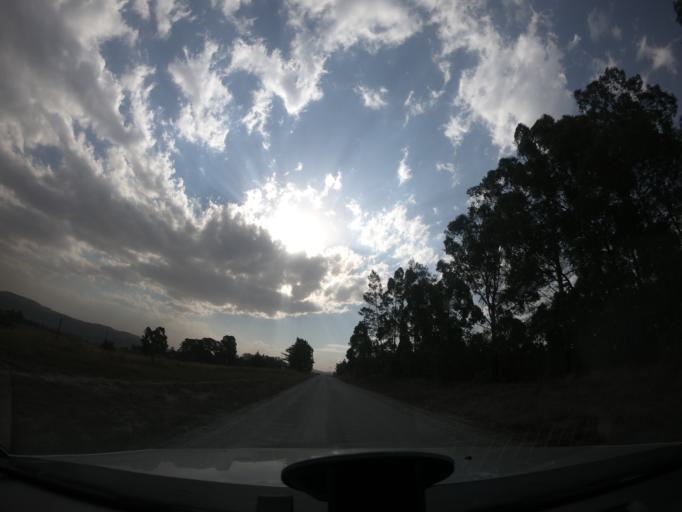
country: ZA
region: KwaZulu-Natal
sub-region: uMgungundlovu District Municipality
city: Howick
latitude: -29.4282
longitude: 30.1081
